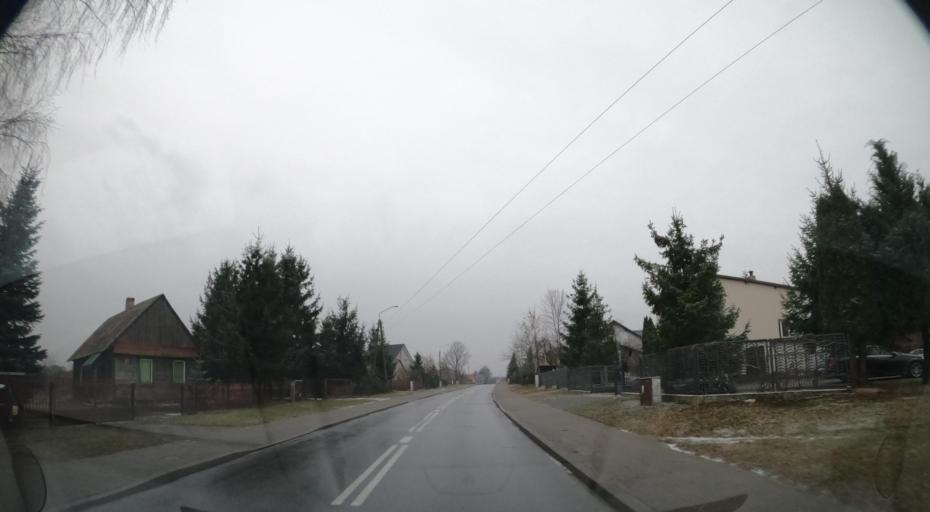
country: PL
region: Masovian Voivodeship
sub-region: Powiat radomski
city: Trablice
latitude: 51.3814
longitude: 21.1051
